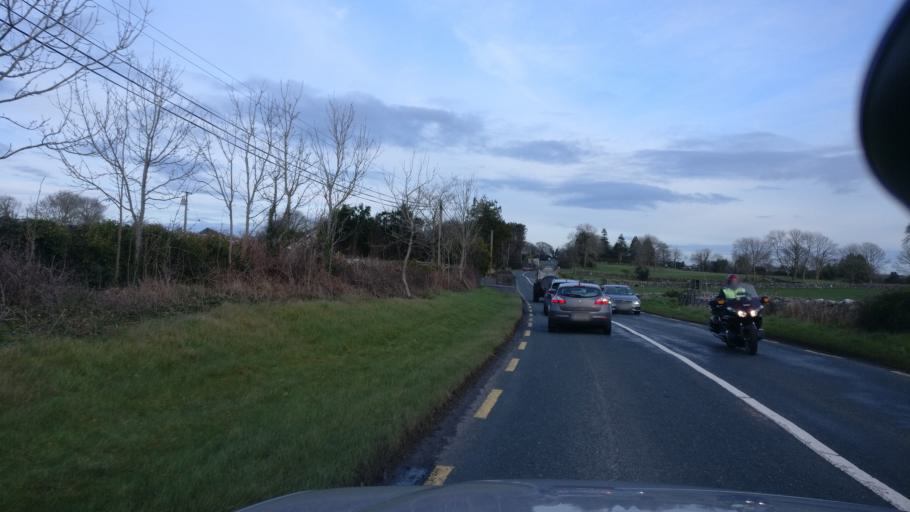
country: IE
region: Connaught
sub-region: Maigh Eo
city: Ballinrobe
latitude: 53.5398
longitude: -9.2355
